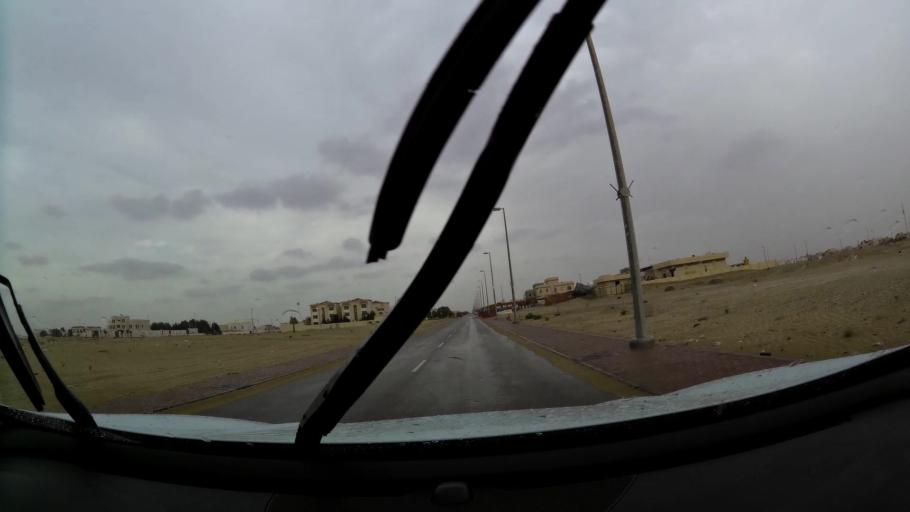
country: AE
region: Abu Dhabi
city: Abu Dhabi
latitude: 24.3664
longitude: 54.6285
